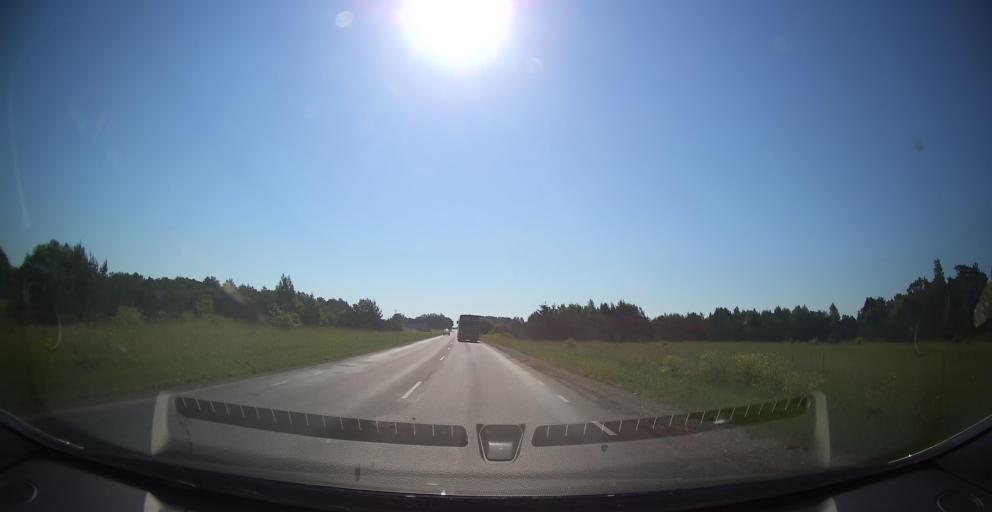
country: EE
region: Harju
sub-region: Raasiku vald
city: Arukula
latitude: 59.3490
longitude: 25.0832
